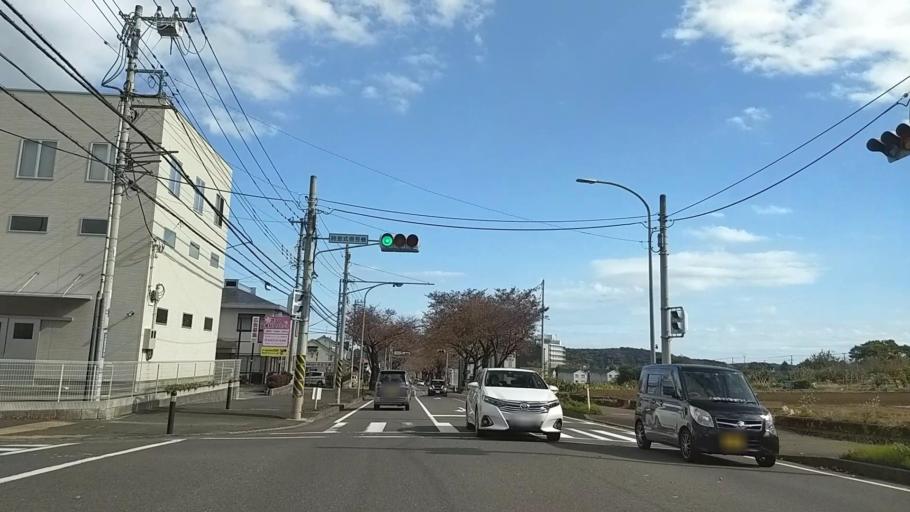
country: JP
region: Kanagawa
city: Hadano
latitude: 35.3621
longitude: 139.2231
